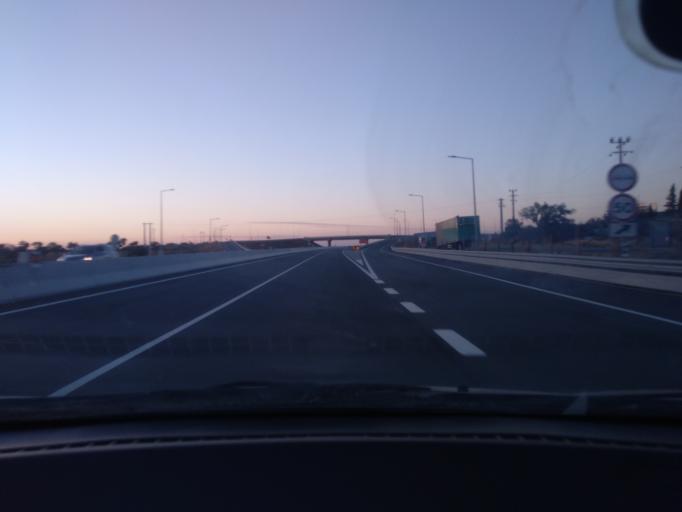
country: PT
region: Beja
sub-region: Beja
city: Beja
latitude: 37.9270
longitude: -7.8712
